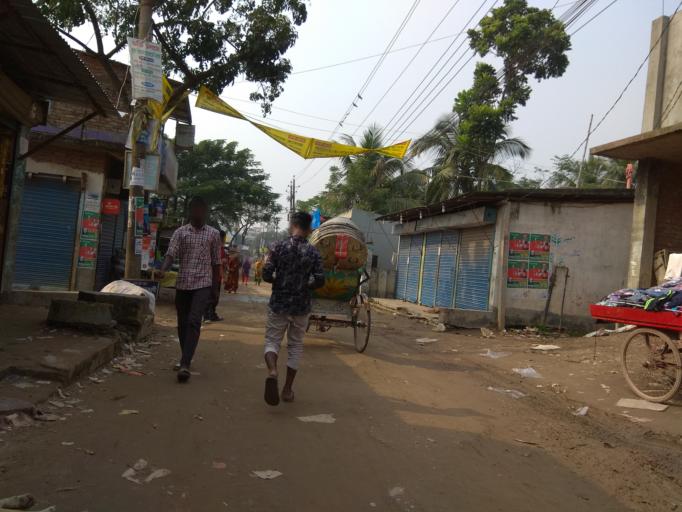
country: BD
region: Dhaka
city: Tungi
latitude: 23.8543
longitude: 90.3858
